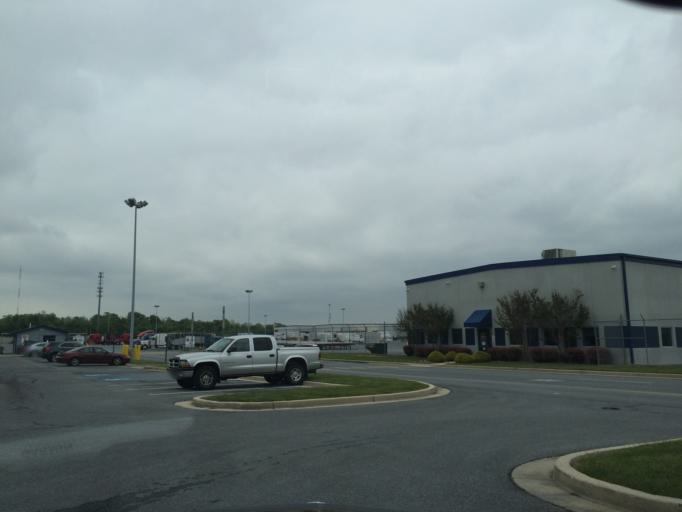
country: US
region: Maryland
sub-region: Washington County
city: Halfway
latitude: 39.6377
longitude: -77.7468
